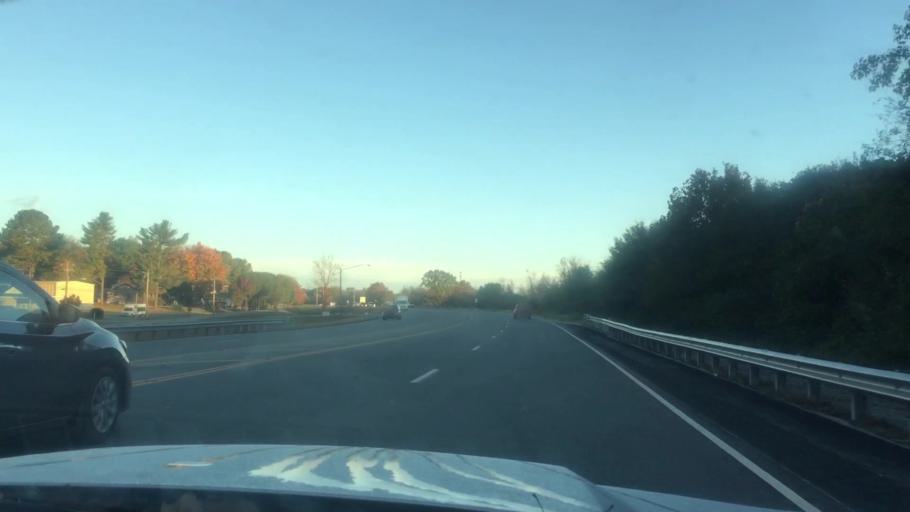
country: US
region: Tennessee
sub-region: Franklin County
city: Estill Springs
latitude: 35.2599
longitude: -86.1217
